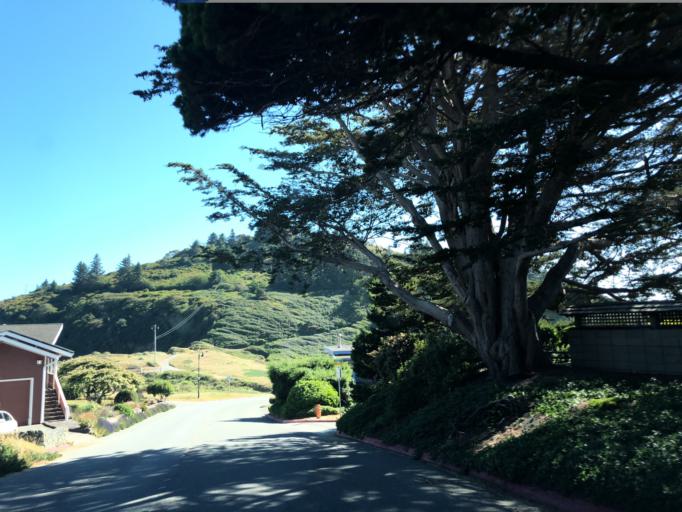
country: US
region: California
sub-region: Humboldt County
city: Westhaven-Moonstone
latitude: 41.0585
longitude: -124.1475
